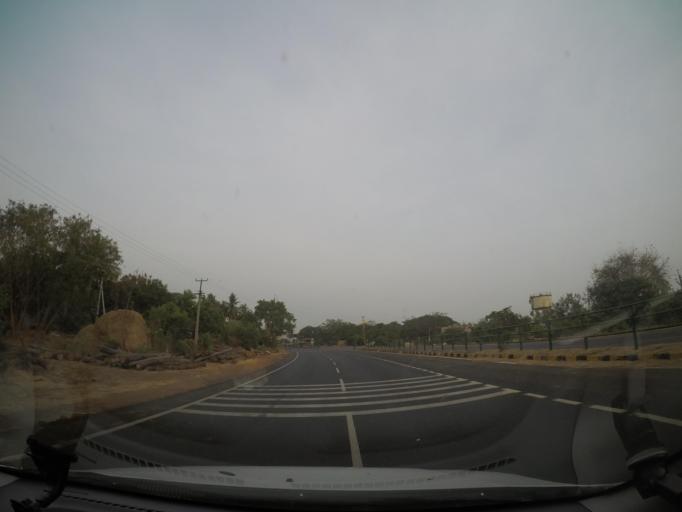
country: IN
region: Andhra Pradesh
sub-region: Krishna
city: Gannavaram
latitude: 16.6109
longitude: 80.9138
